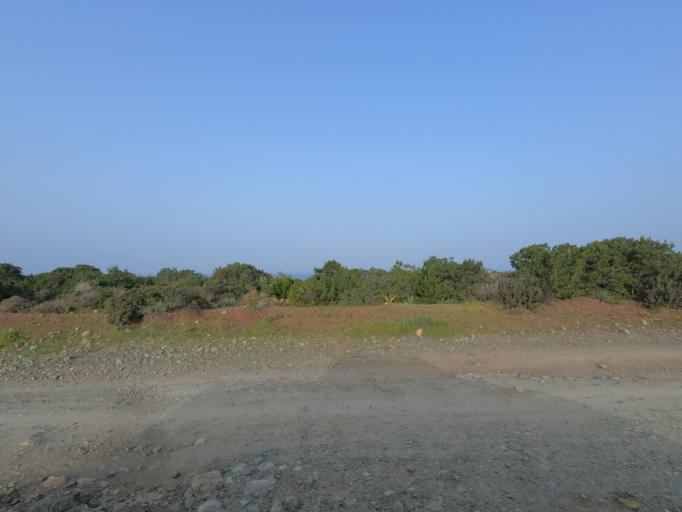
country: CY
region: Pafos
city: Pegeia
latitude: 34.9738
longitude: 32.3138
